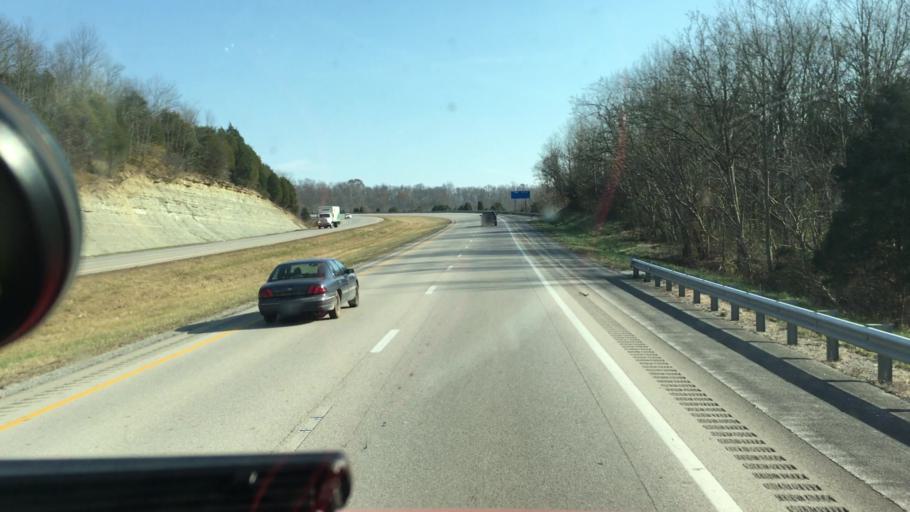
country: US
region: Kentucky
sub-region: Bath County
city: Owingsville
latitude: 38.1226
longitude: -83.7682
